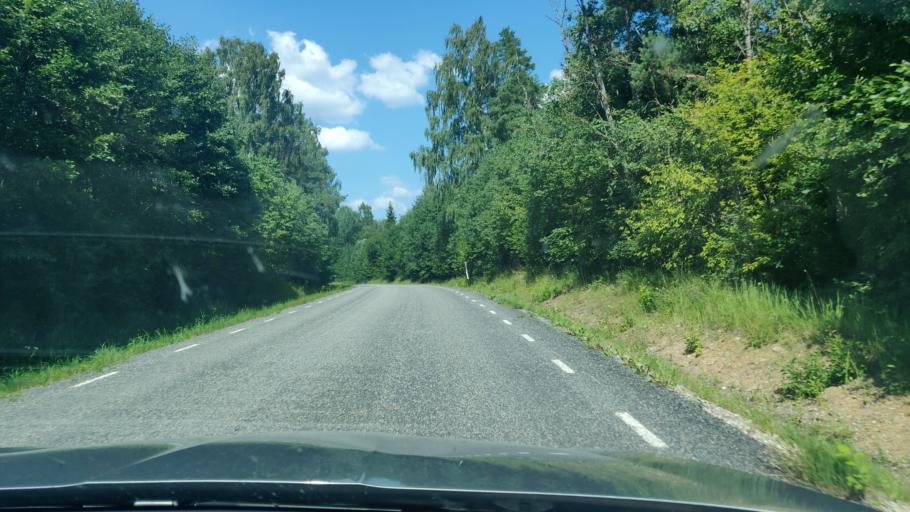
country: EE
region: Tartu
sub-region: Elva linn
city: Elva
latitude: 58.1507
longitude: 26.4733
